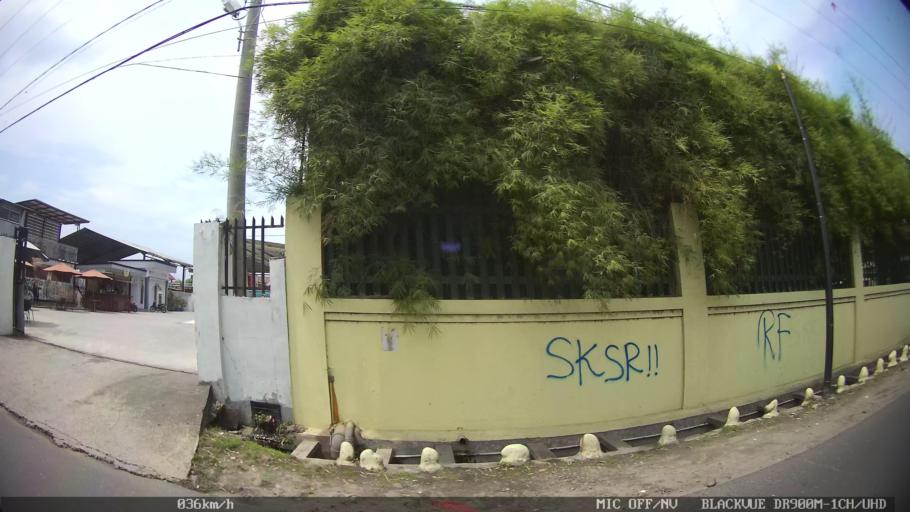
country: ID
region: North Sumatra
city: Medan
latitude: 3.6430
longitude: 98.6703
